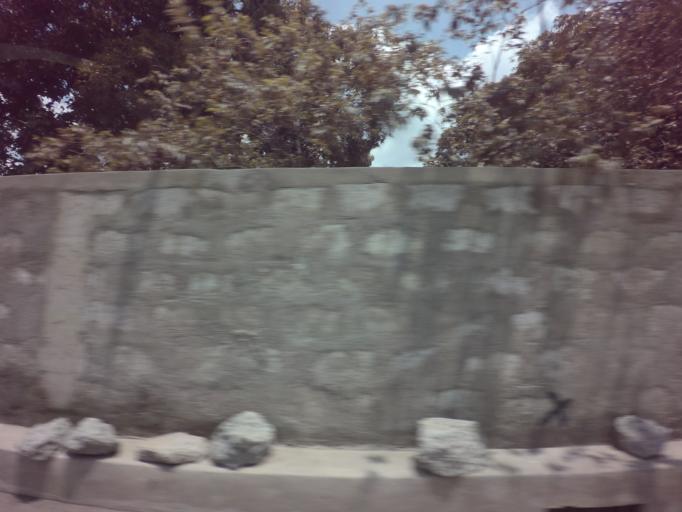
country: PH
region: Calabarzon
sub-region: Province of Laguna
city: San Pedro
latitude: 14.3849
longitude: 121.0511
